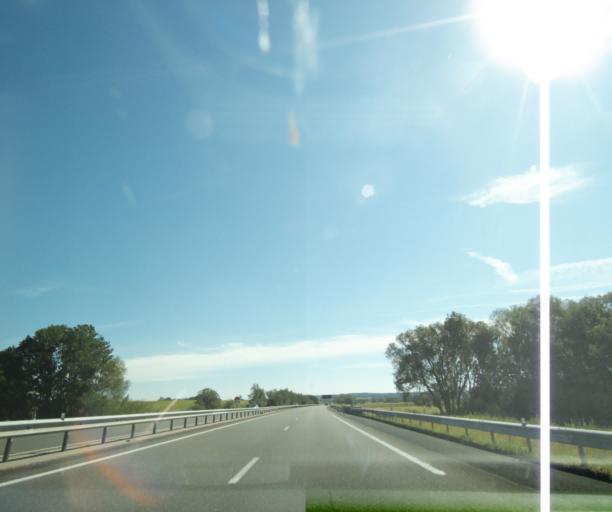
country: FR
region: Lorraine
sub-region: Departement des Vosges
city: Bulgneville
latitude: 48.2053
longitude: 5.8026
